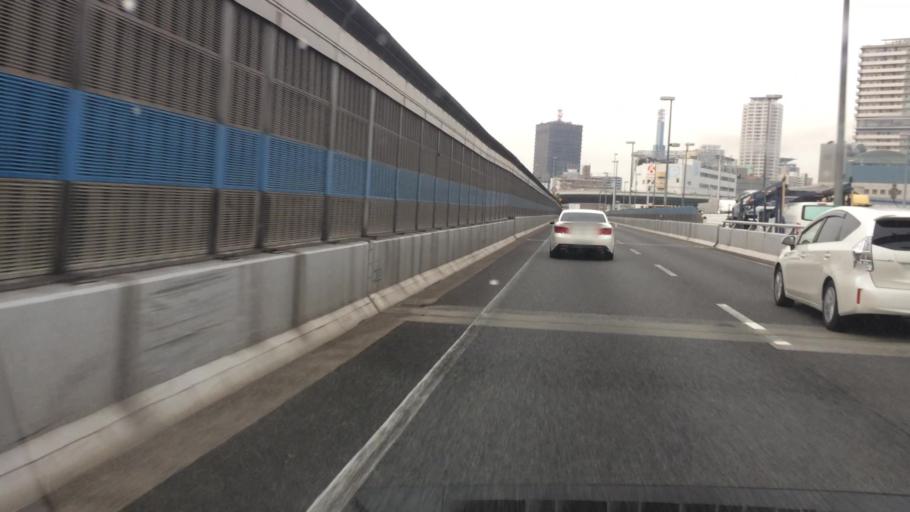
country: JP
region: Hyogo
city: Kobe
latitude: 34.6950
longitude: 135.2052
